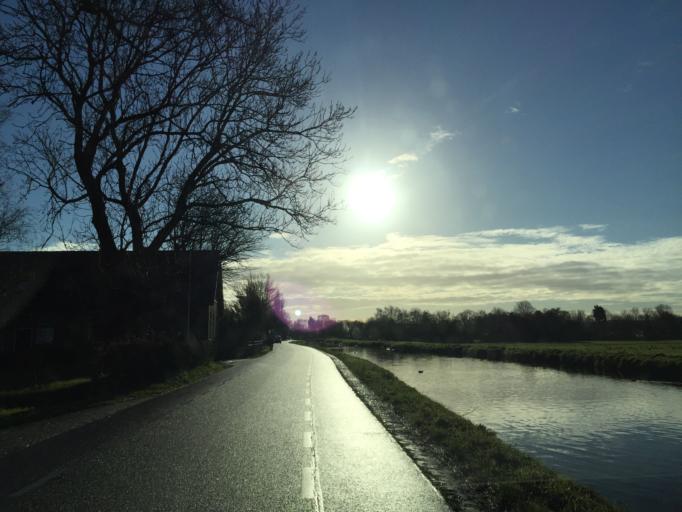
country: NL
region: South Holland
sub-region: Gemeente Pijnacker-Nootdorp
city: Pijnacker
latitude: 52.0333
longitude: 4.4292
